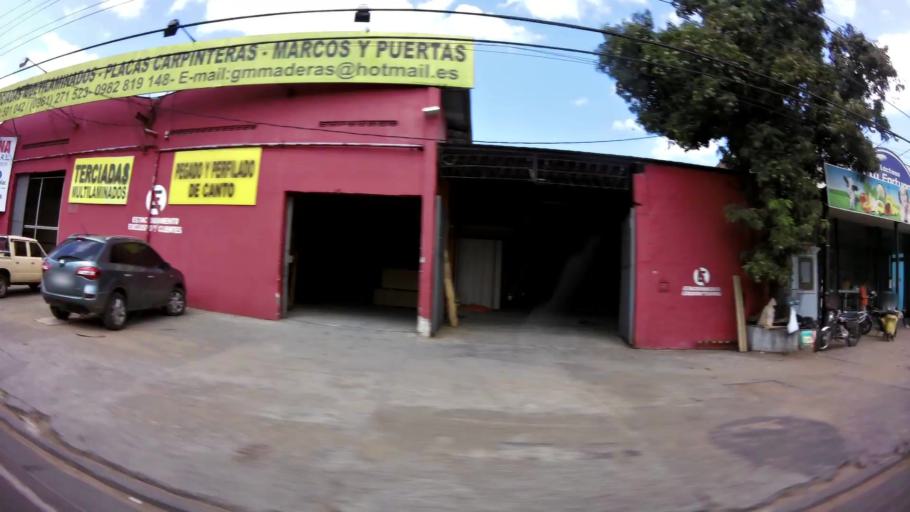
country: PY
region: Central
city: Fernando de la Mora
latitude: -25.3171
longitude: -57.5578
